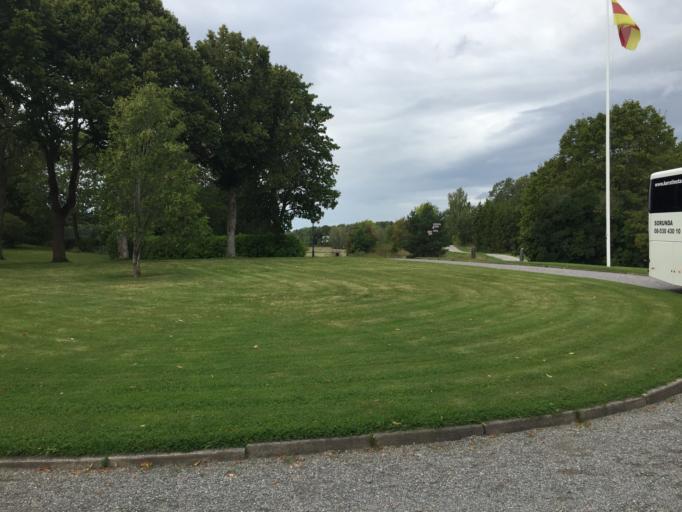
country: SE
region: Stockholm
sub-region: Norrtalje Kommun
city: Rimbo
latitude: 59.7328
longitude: 18.5010
